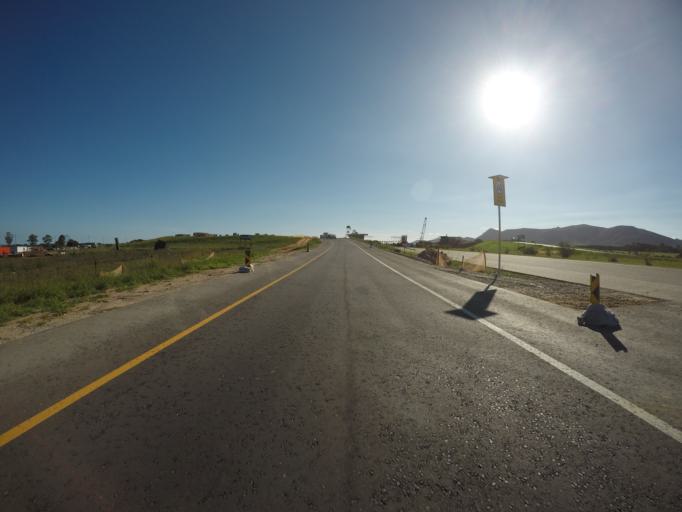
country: ZA
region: Eastern Cape
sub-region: Nelson Mandela Bay Metropolitan Municipality
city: Uitenhage
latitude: -33.9198
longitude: 25.2955
